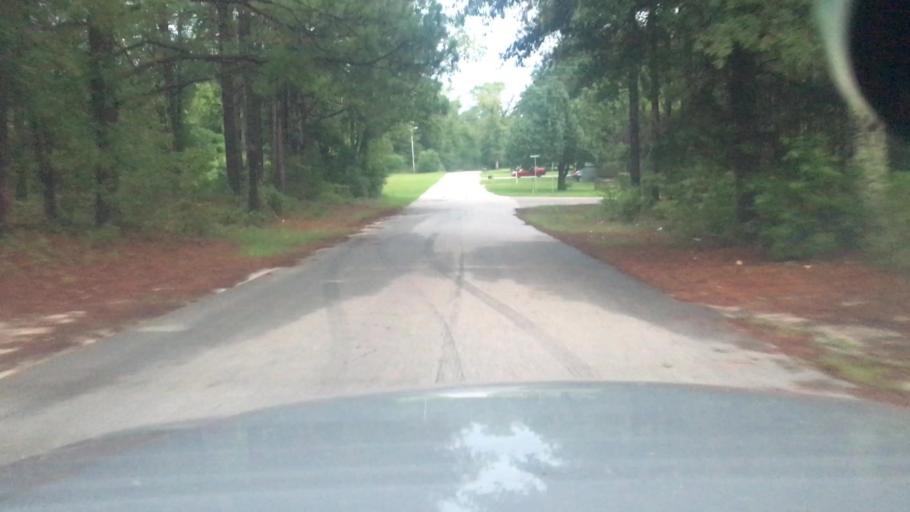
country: US
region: North Carolina
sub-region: Cumberland County
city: Hope Mills
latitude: 34.9650
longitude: -78.9302
